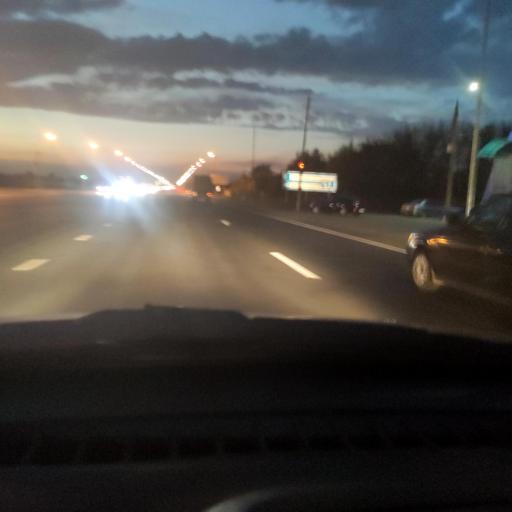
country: RU
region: Samara
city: Tol'yatti
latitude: 53.5727
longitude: 49.4608
